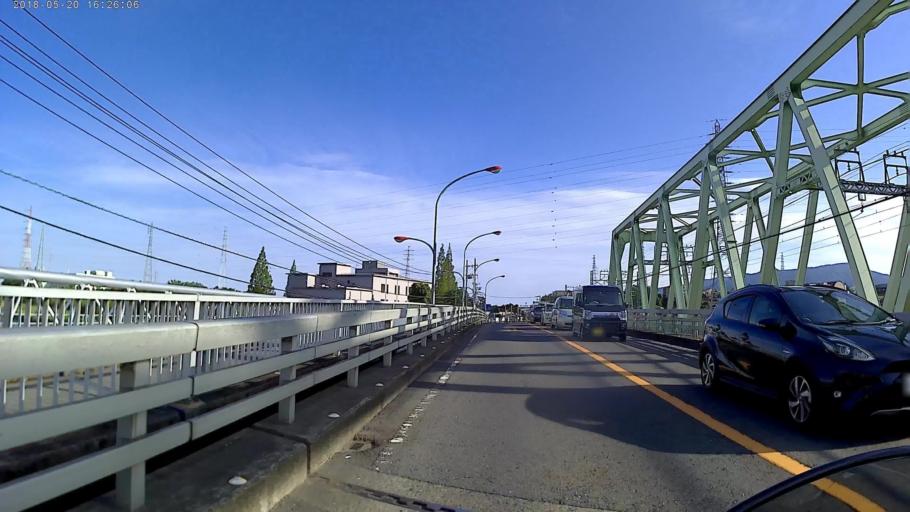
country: JP
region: Kanagawa
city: Odawara
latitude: 35.2799
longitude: 139.1553
